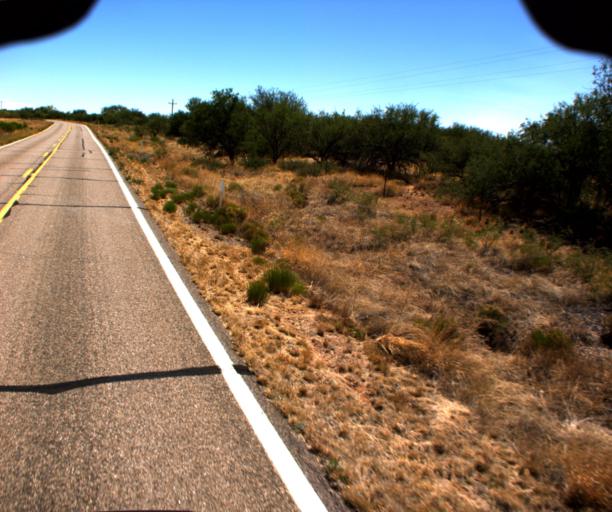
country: US
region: Arizona
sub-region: Pima County
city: Three Points
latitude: 31.7332
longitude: -111.4871
